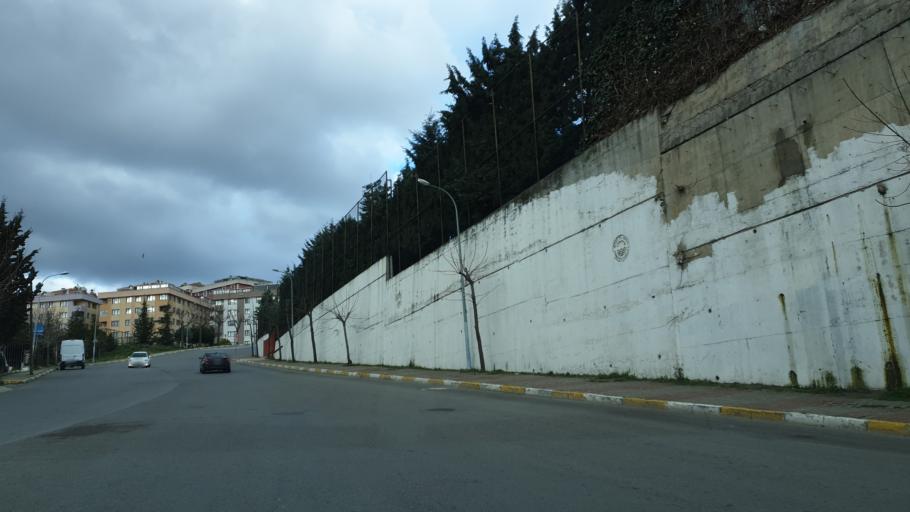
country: TR
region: Istanbul
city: Pendik
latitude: 40.8996
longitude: 29.2451
